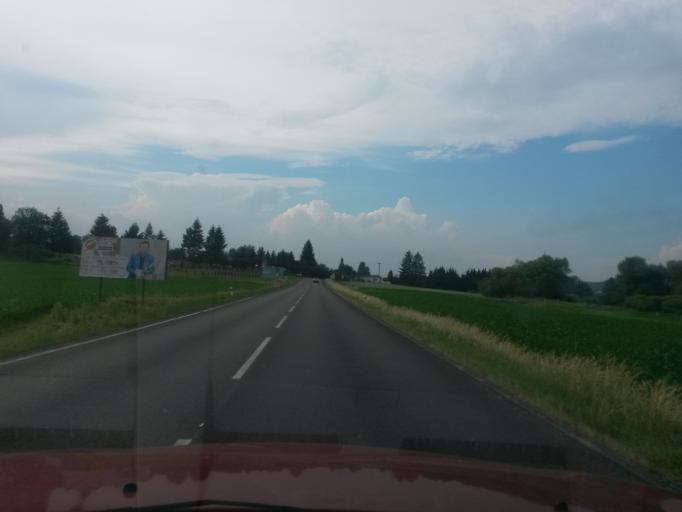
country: SK
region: Presovsky
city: Vranov nad Topl'ou
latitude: 48.9005
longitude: 21.6361
